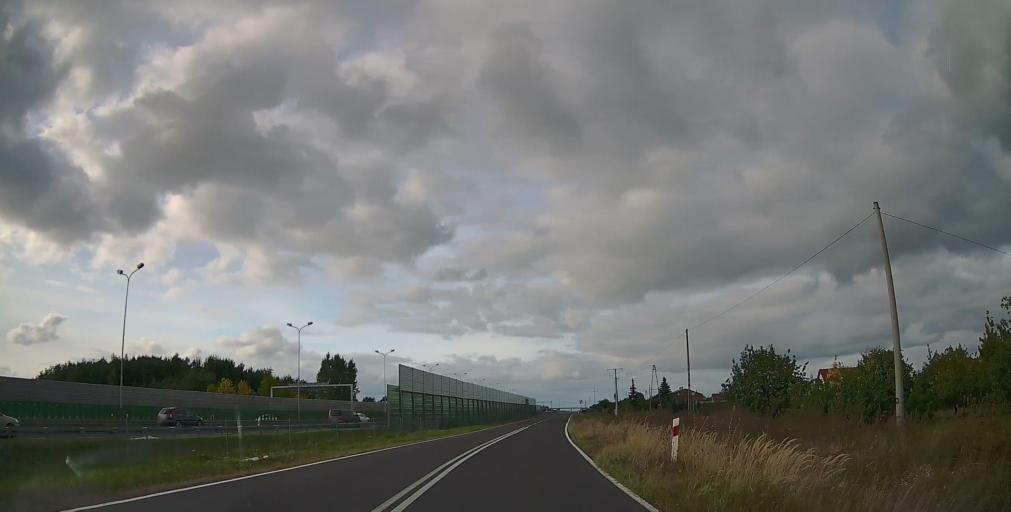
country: PL
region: Masovian Voivodeship
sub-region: Powiat grojecki
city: Goszczyn
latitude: 51.7625
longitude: 20.8989
